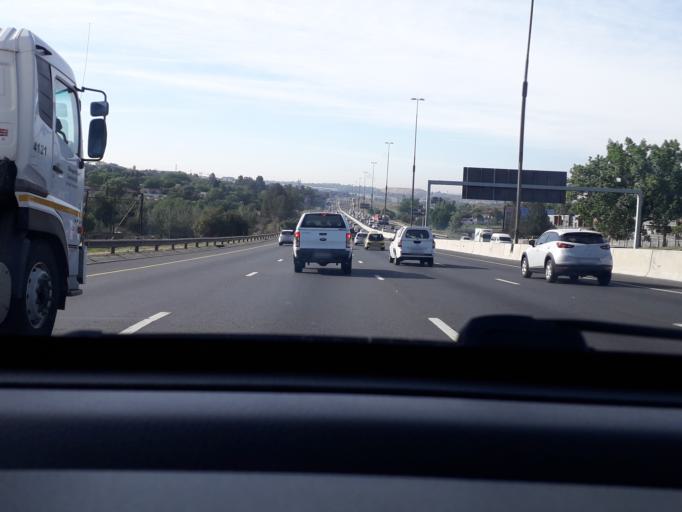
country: ZA
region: Gauteng
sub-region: City of Johannesburg Metropolitan Municipality
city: Midrand
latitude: -26.0523
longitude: 28.1023
